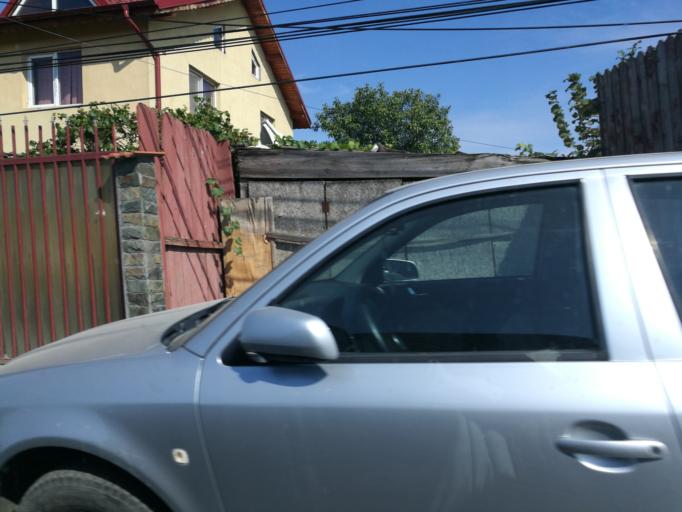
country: RO
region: Ilfov
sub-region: Comuna Otopeni
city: Otopeni
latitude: 44.5481
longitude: 26.0804
